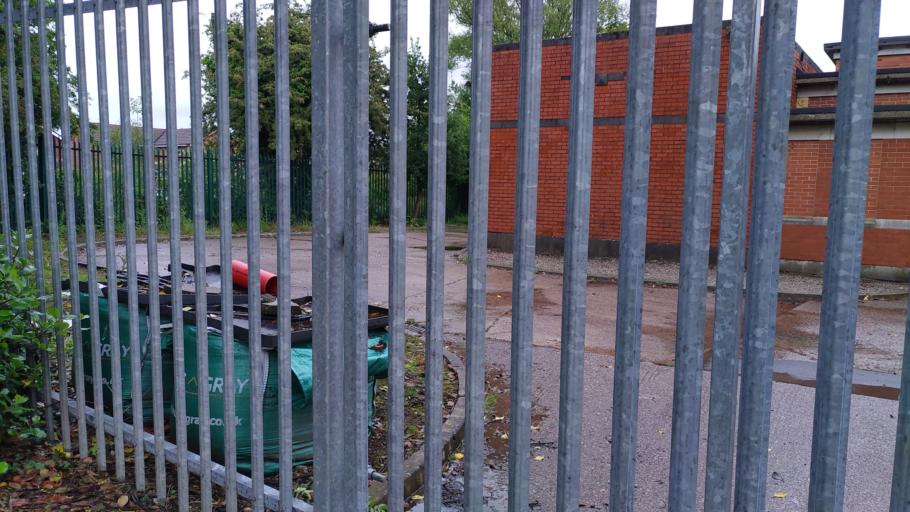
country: GB
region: England
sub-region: Lancashire
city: Appley Bridge
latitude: 53.6142
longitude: -2.7048
